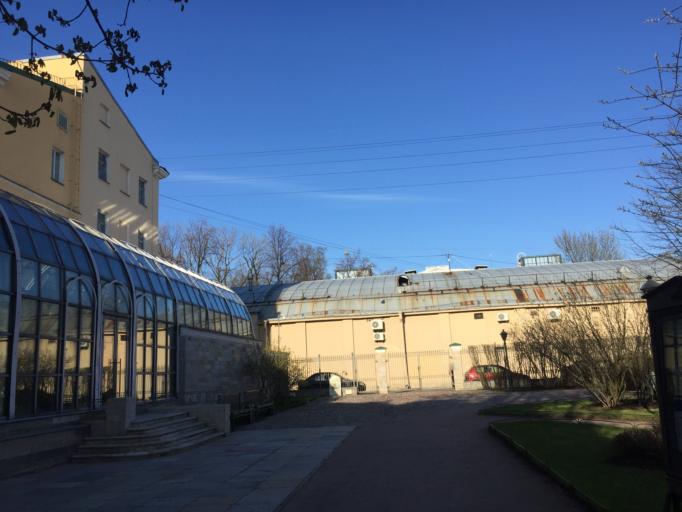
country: RU
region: St.-Petersburg
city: Saint Petersburg
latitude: 59.9189
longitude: 30.3114
